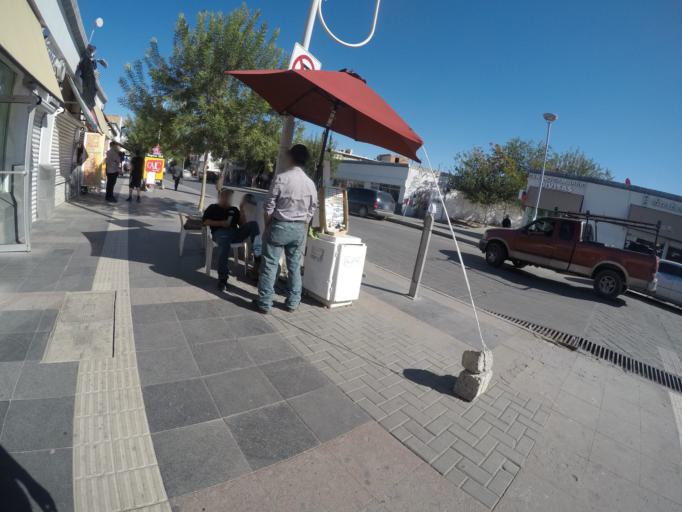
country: MX
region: Chihuahua
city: Ciudad Juarez
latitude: 31.7418
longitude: -106.4854
